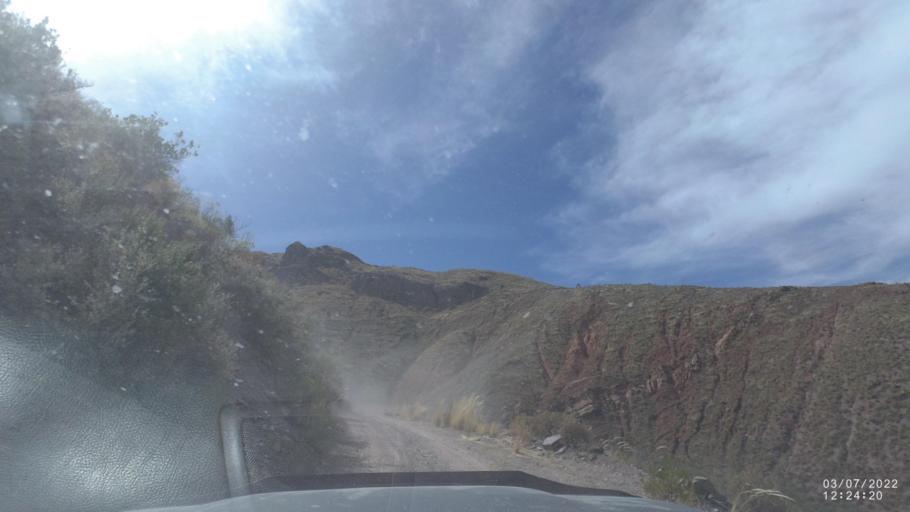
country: BO
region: Cochabamba
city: Irpa Irpa
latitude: -17.8134
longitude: -66.6174
